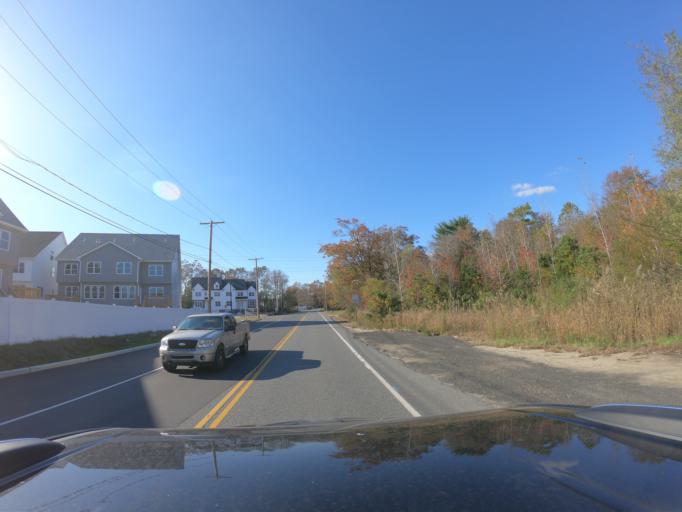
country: US
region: New Jersey
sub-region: Monmouth County
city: Ramtown
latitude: 40.0919
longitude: -74.1540
